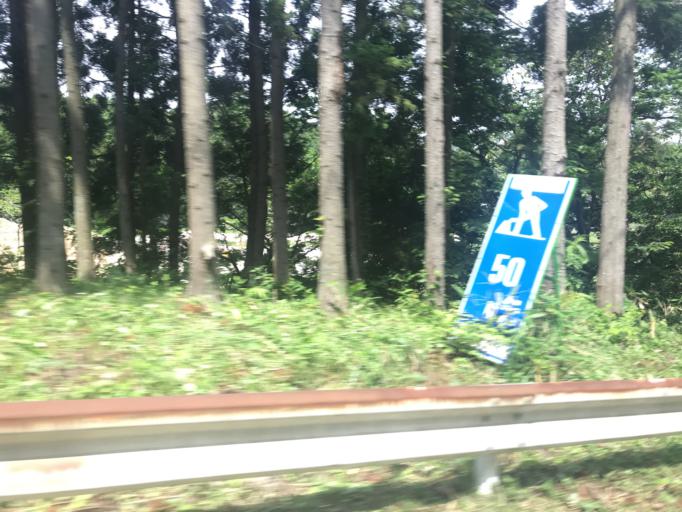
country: JP
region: Fukushima
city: Namie
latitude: 37.3046
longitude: 141.0213
